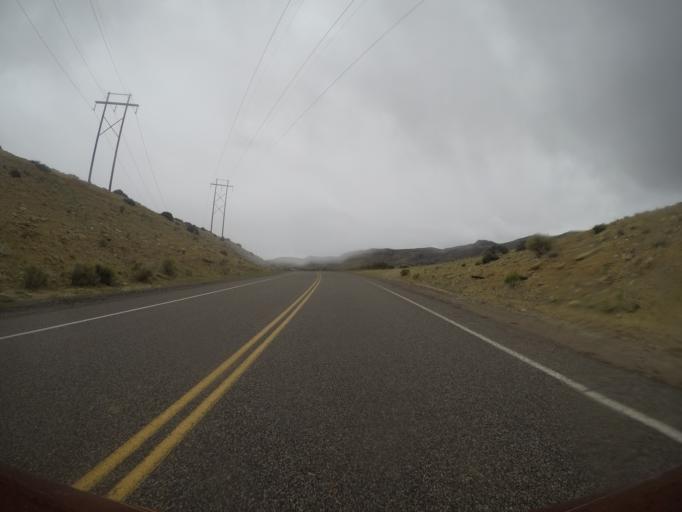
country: US
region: Wyoming
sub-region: Big Horn County
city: Lovell
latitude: 45.0248
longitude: -108.2684
